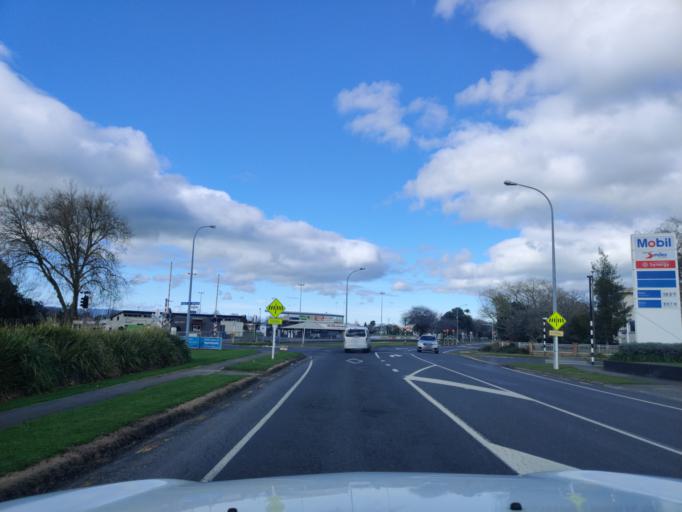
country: NZ
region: Waikato
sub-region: Matamata-Piako District
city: Matamata
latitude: -37.8142
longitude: 175.7709
